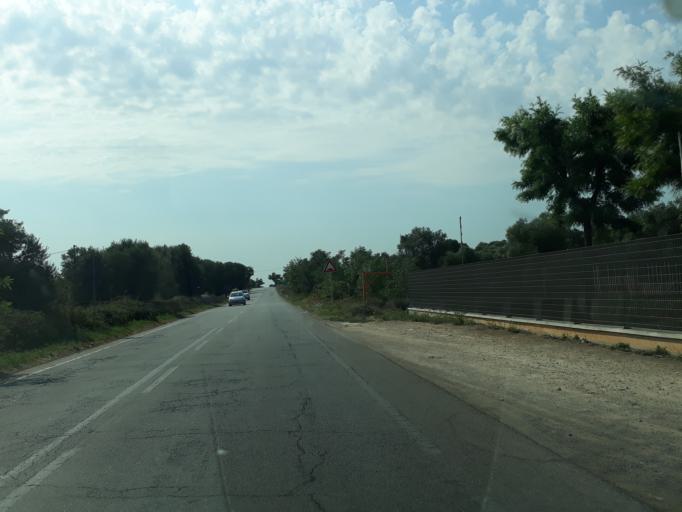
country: IT
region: Apulia
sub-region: Provincia di Brindisi
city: Carovigno
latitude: 40.6941
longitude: 17.6703
